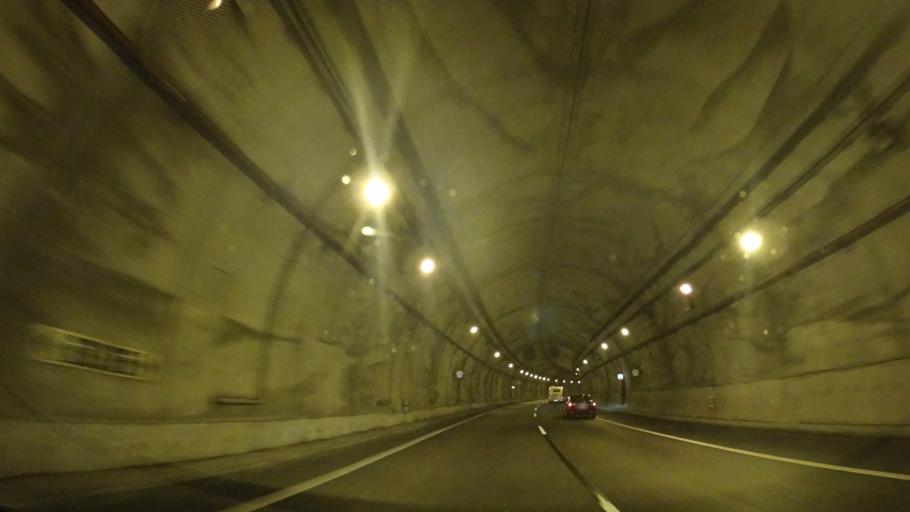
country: ES
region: Asturias
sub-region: Province of Asturias
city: Arriba
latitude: 43.4634
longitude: -5.5152
